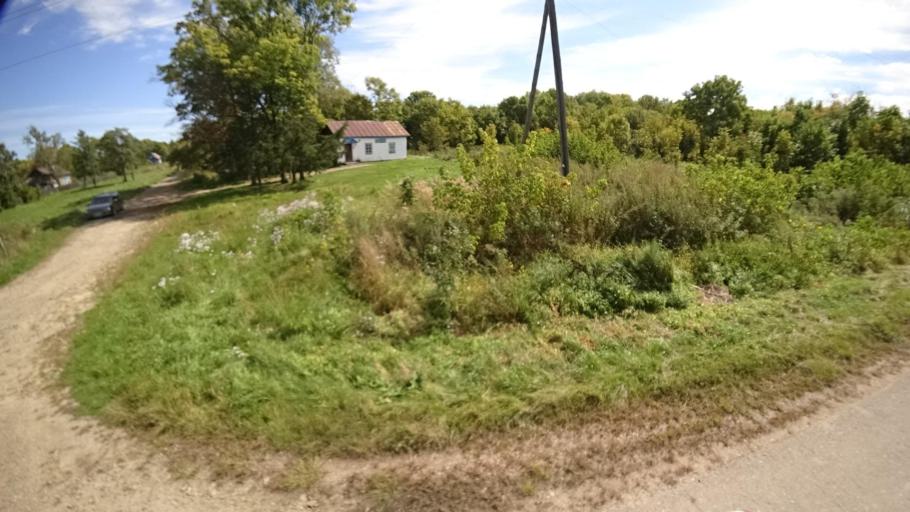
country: RU
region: Primorskiy
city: Yakovlevka
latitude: 44.7521
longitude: 133.6063
